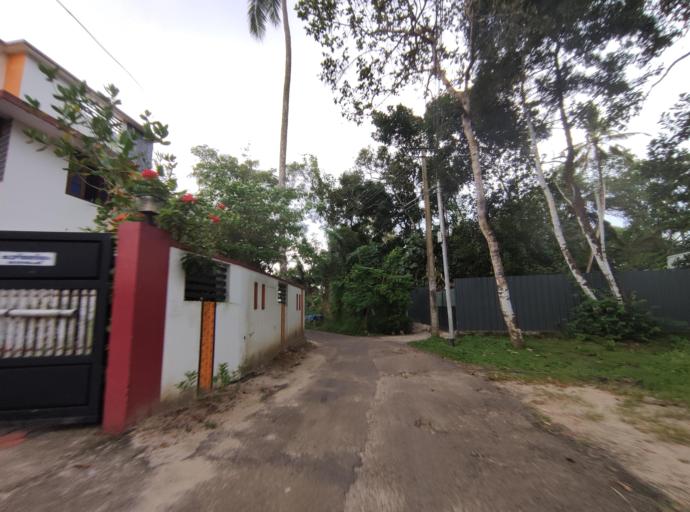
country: IN
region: Kerala
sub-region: Alappuzha
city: Shertallai
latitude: 9.6682
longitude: 76.3350
